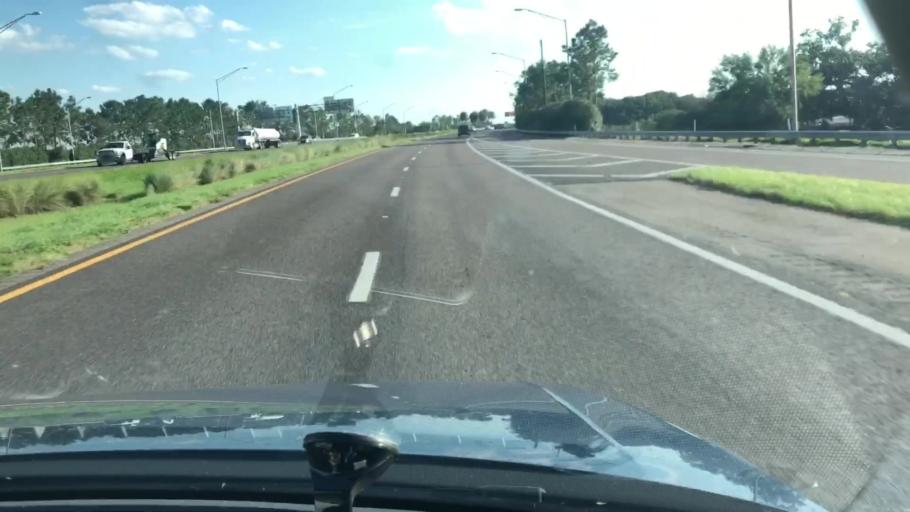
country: US
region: Florida
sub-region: Orange County
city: Ocoee
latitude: 28.5417
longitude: -81.5571
